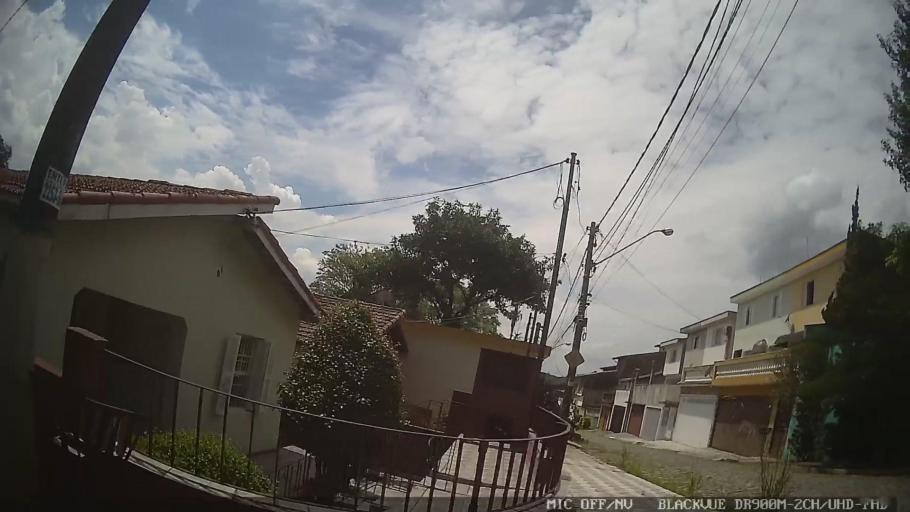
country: BR
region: Sao Paulo
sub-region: Ribeirao Pires
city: Ribeirao Pires
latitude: -23.7185
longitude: -46.4207
